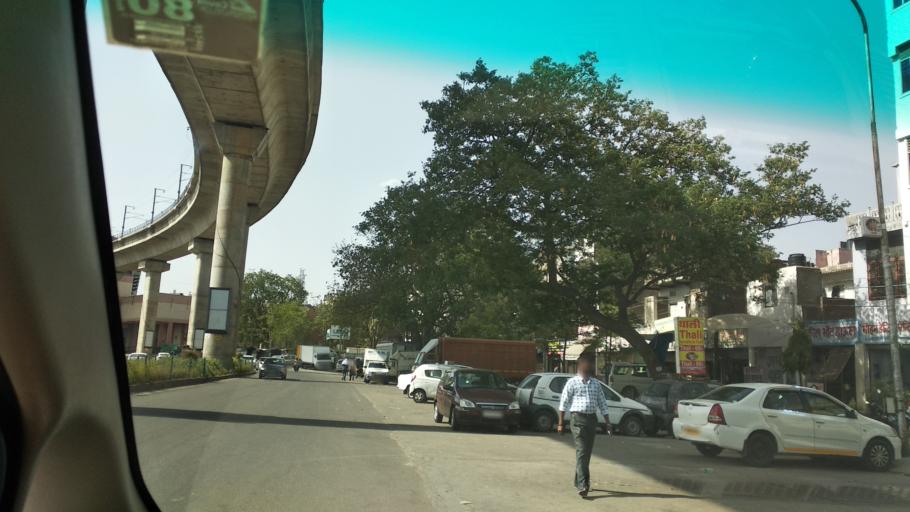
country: IN
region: Rajasthan
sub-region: Jaipur
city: Jaipur
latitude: 26.9158
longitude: 75.7910
